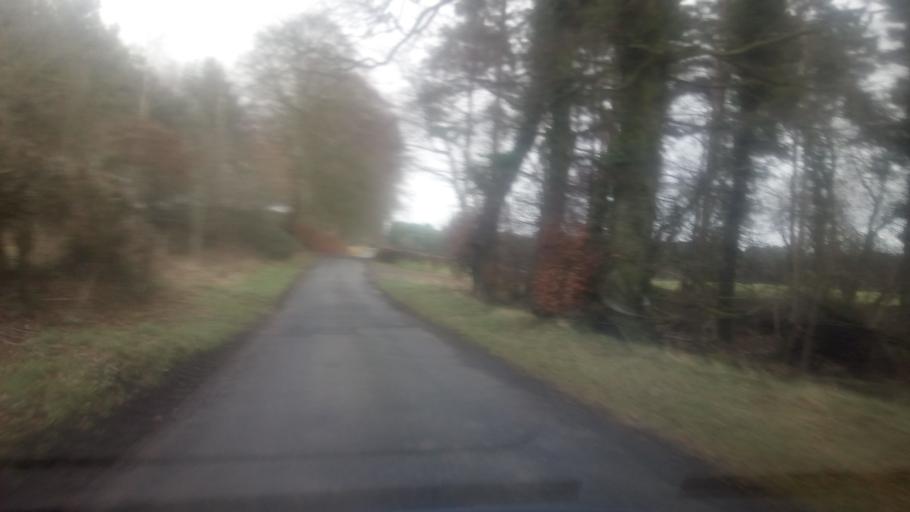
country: GB
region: Scotland
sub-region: The Scottish Borders
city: Jedburgh
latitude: 55.5394
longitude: -2.4956
